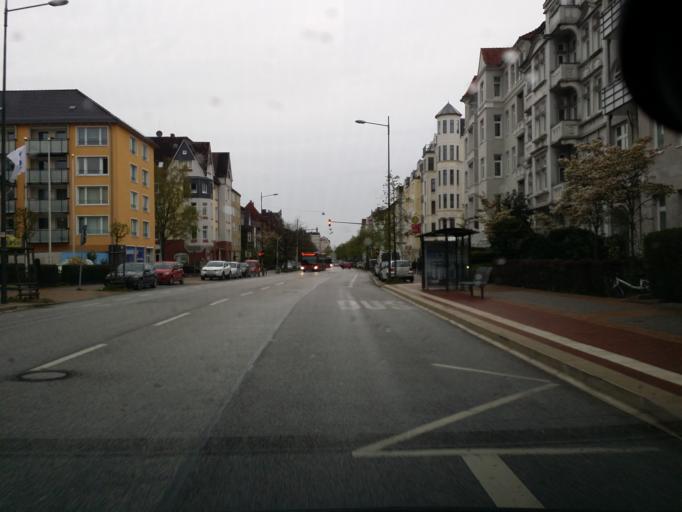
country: DE
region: Schleswig-Holstein
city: Kiel
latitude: 54.3418
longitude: 10.1336
